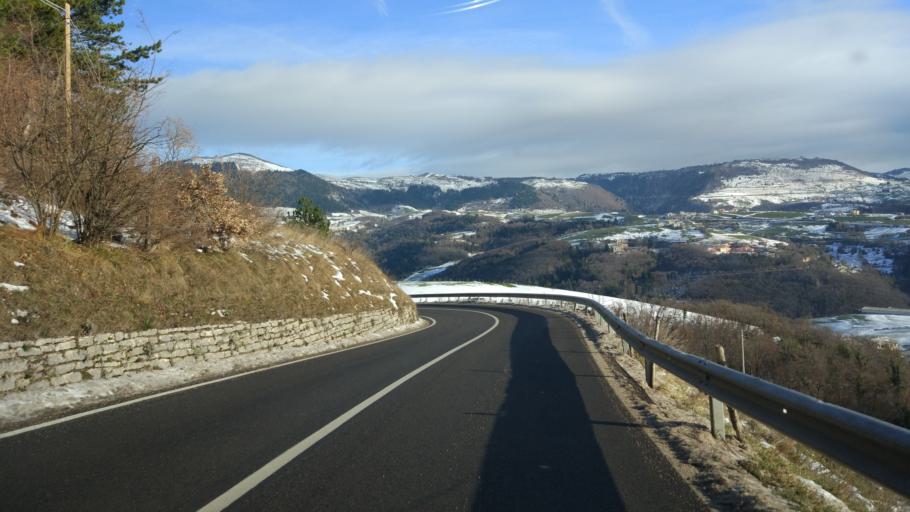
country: IT
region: Veneto
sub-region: Provincia di Verona
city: Sant'Anna d'Alfaedo
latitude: 45.6340
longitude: 10.9424
